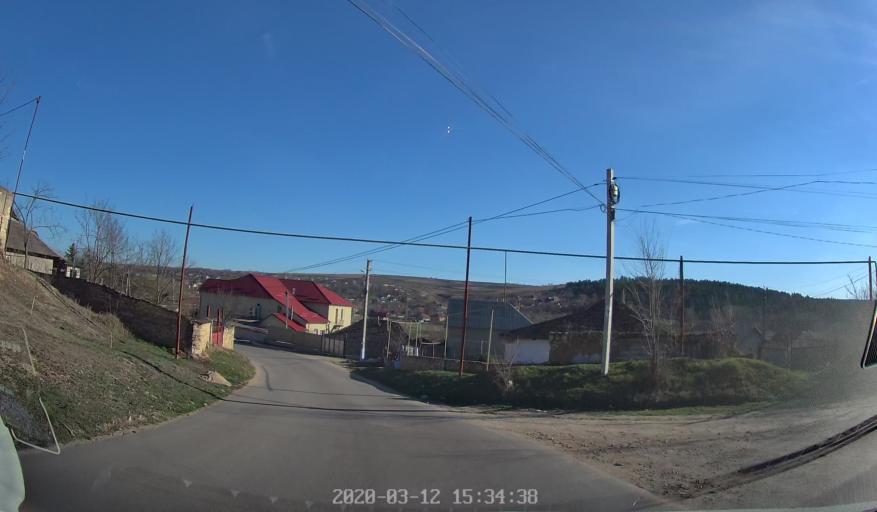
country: MD
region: Chisinau
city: Ciorescu
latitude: 47.1368
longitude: 28.9388
